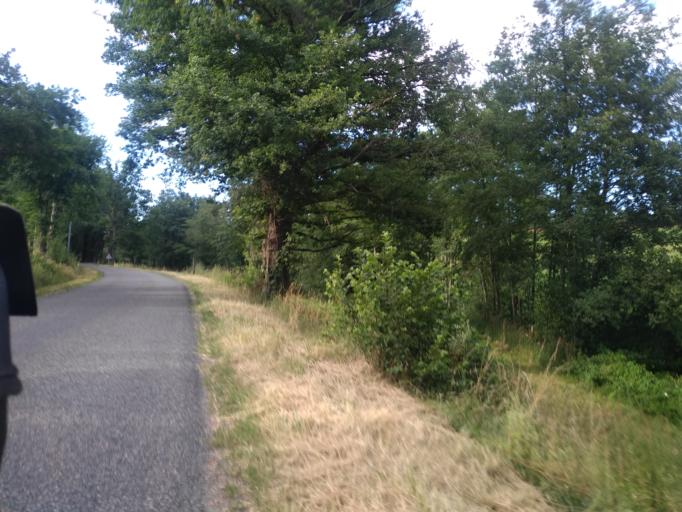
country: FR
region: Rhone-Alpes
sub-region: Departement du Rhone
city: Haute-Rivoire
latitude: 45.7376
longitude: 4.3506
